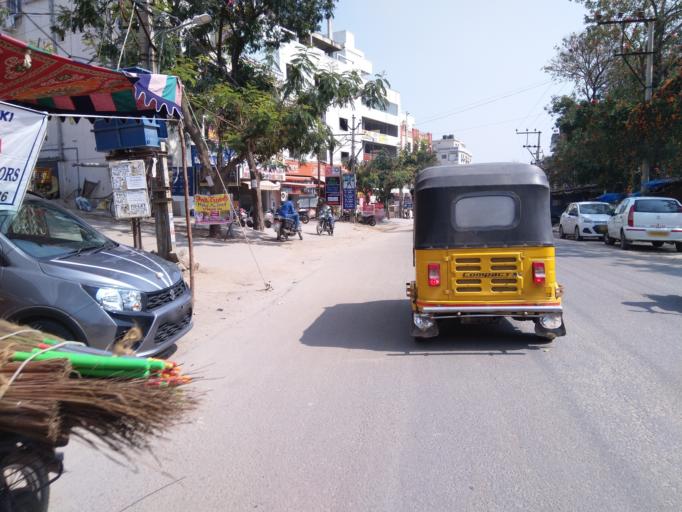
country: IN
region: Telangana
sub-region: Rangareddi
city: Kukatpalli
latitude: 17.4979
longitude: 78.4090
